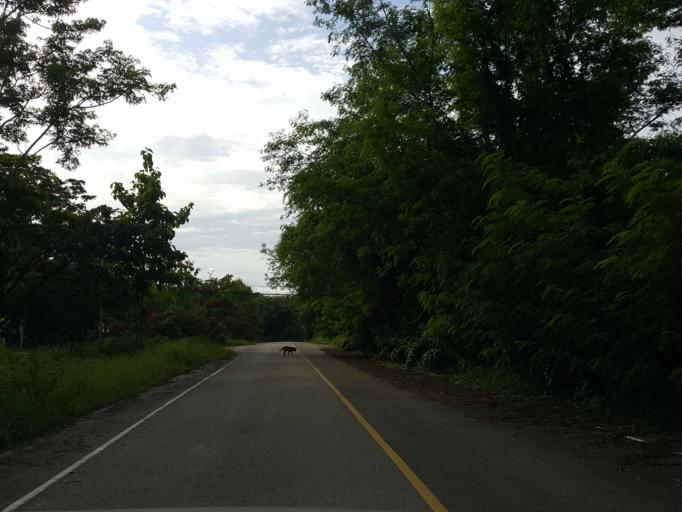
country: TH
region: Chiang Mai
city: San Sai
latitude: 18.9372
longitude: 99.1427
